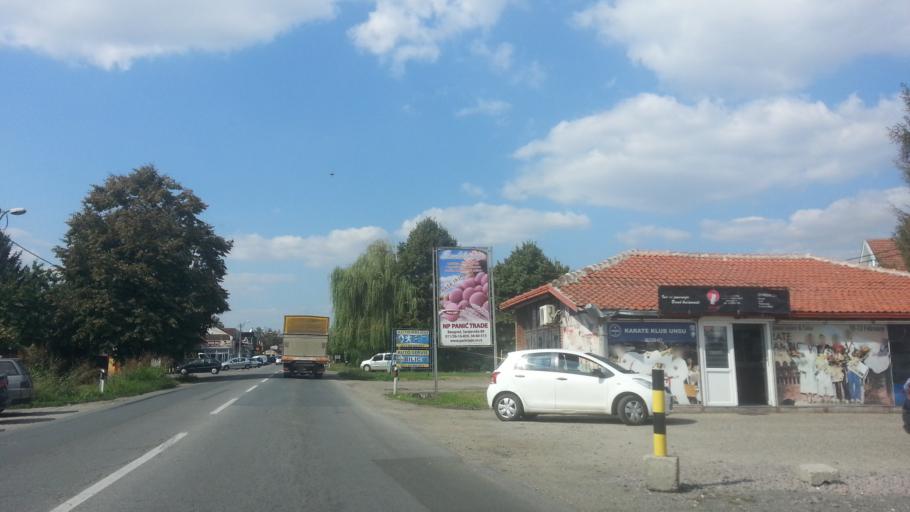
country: RS
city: Novi Banovci
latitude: 44.8955
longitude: 20.2953
